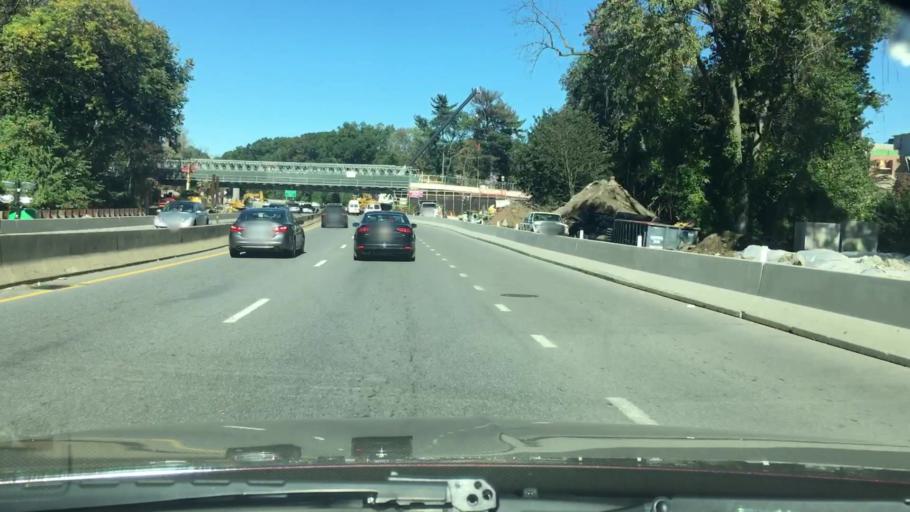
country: US
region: New York
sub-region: Westchester County
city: Pelham
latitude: 40.9045
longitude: -73.8139
